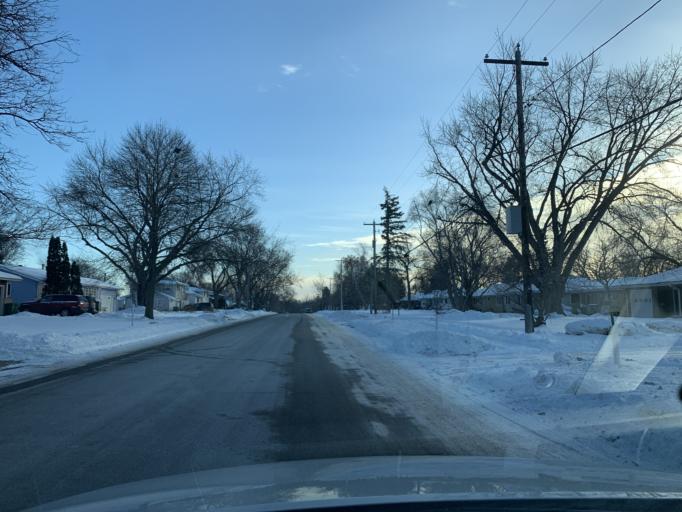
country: US
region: Minnesota
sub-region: Hennepin County
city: Minnetonka Mills
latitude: 44.9593
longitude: -93.3962
